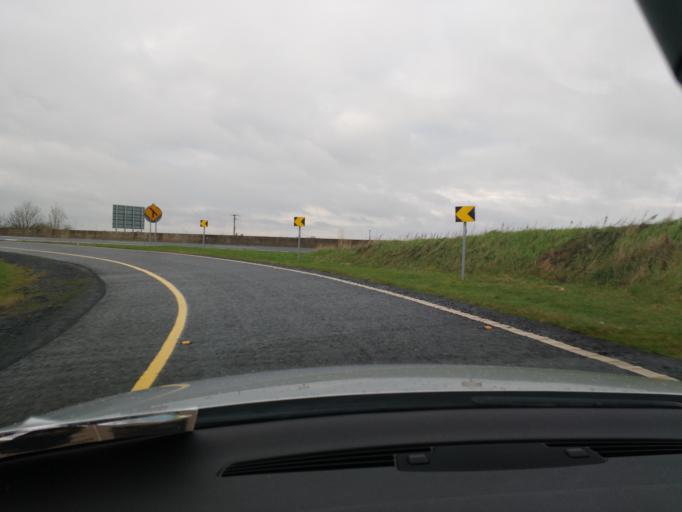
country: IE
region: Munster
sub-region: North Tipperary
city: Nenagh
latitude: 52.8503
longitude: -8.1535
